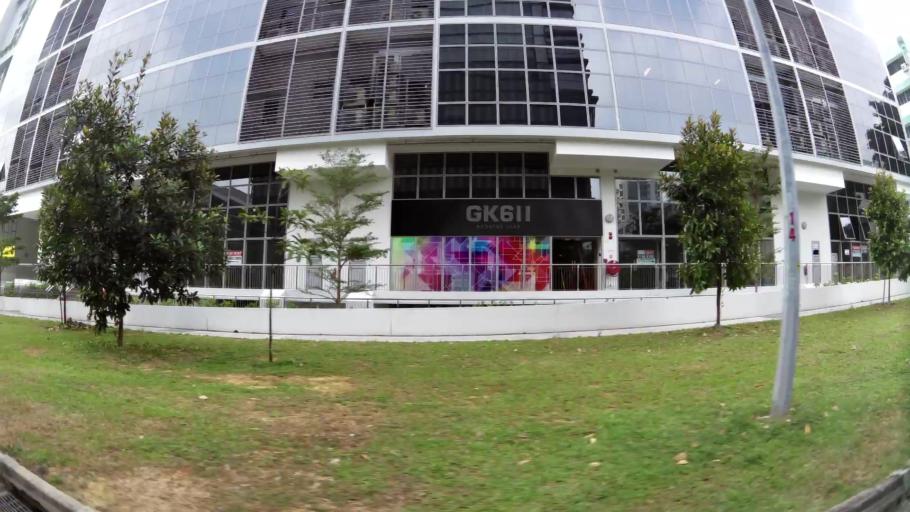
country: SG
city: Singapore
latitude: 1.3488
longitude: 103.8412
